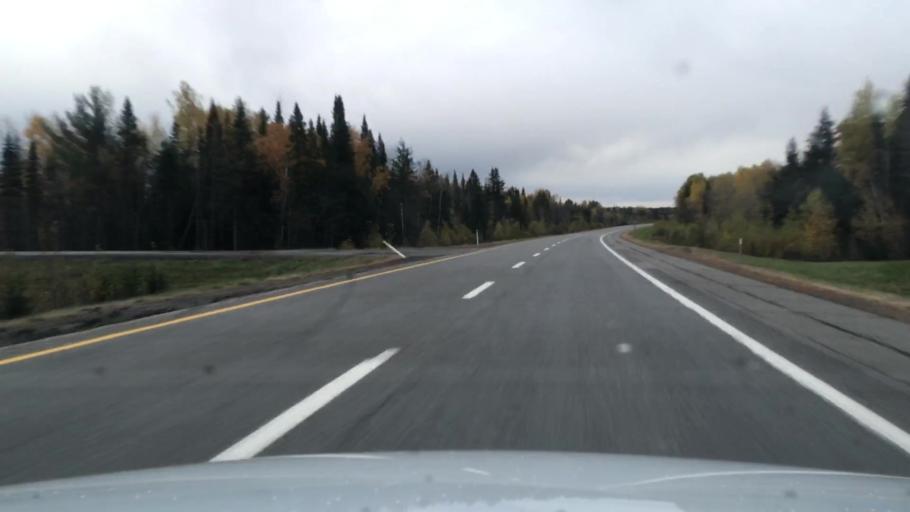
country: US
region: Maine
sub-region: Penobscot County
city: Greenbush
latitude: 45.1226
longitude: -68.6954
